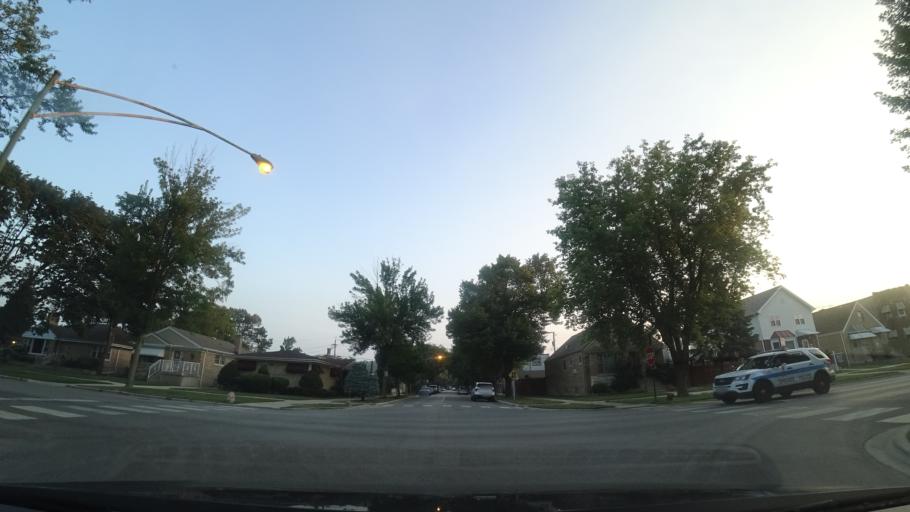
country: US
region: Illinois
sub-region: Cook County
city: Harwood Heights
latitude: 41.9622
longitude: -87.7698
